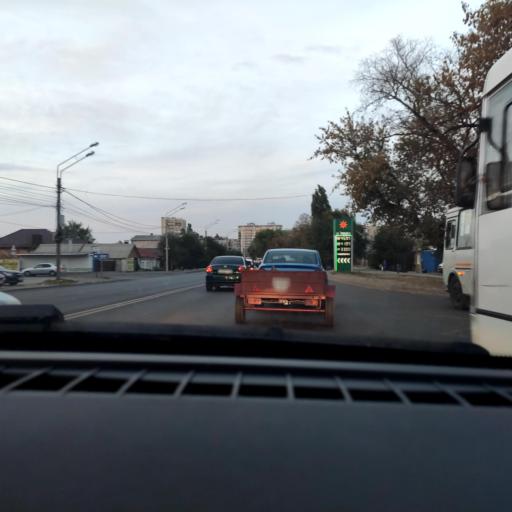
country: RU
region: Voronezj
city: Voronezh
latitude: 51.6570
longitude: 39.2750
